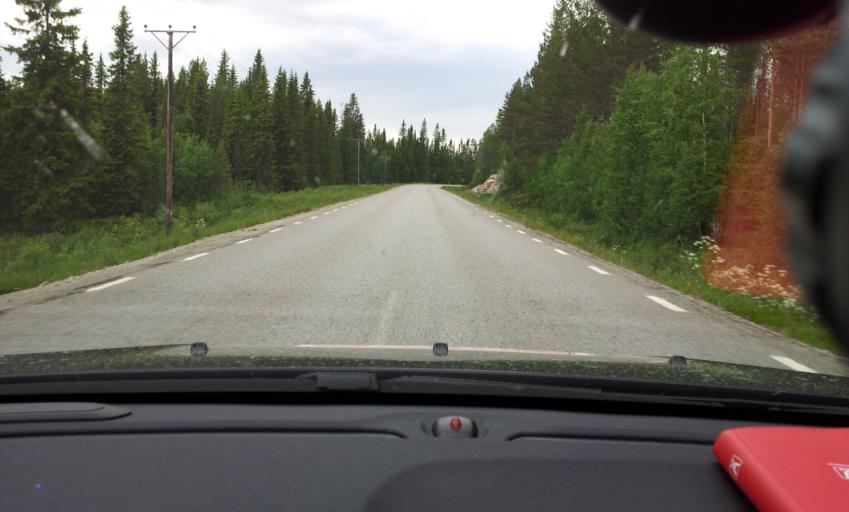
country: SE
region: Jaemtland
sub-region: Bergs Kommun
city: Hoverberg
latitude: 62.6761
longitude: 14.6786
